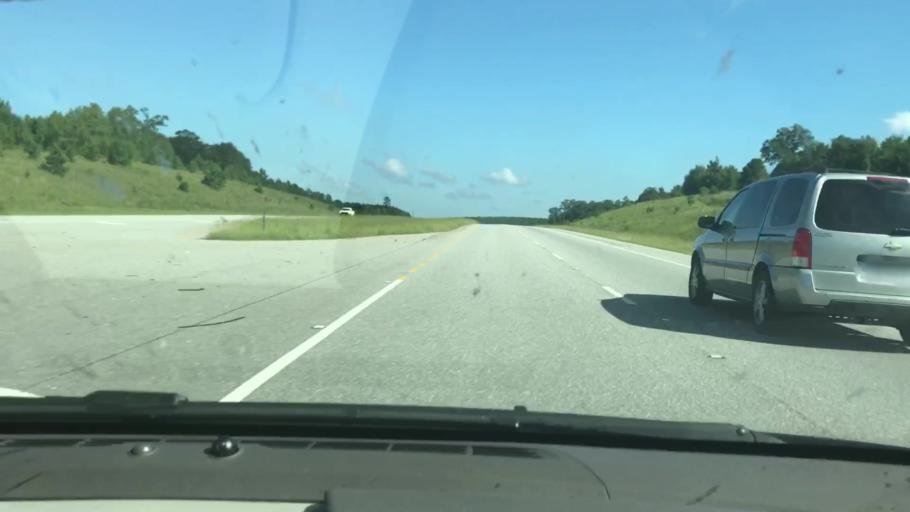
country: US
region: Alabama
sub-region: Barbour County
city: Eufaula
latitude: 32.1047
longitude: -85.1501
